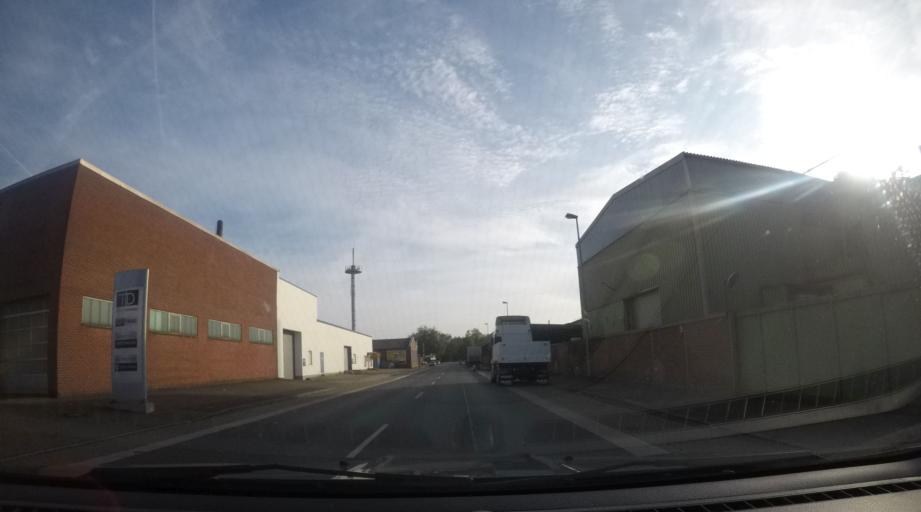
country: DE
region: North Rhine-Westphalia
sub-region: Regierungsbezirk Dusseldorf
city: Bocholt
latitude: 51.8291
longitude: 6.6298
